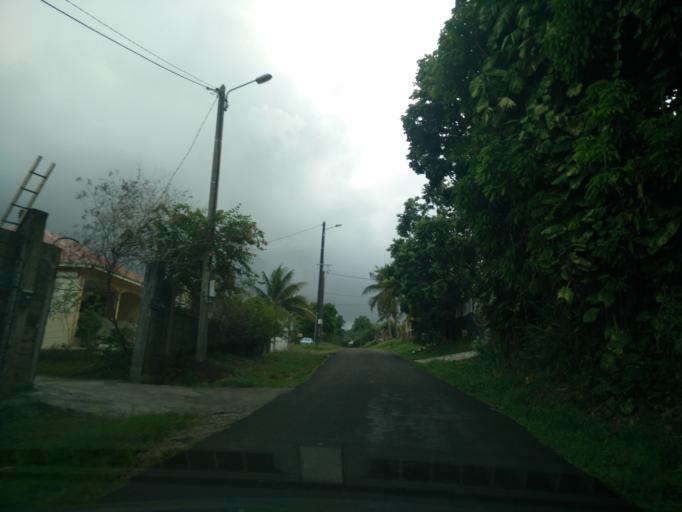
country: GP
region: Guadeloupe
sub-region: Guadeloupe
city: Petit-Bourg
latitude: 16.1803
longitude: -61.6129
